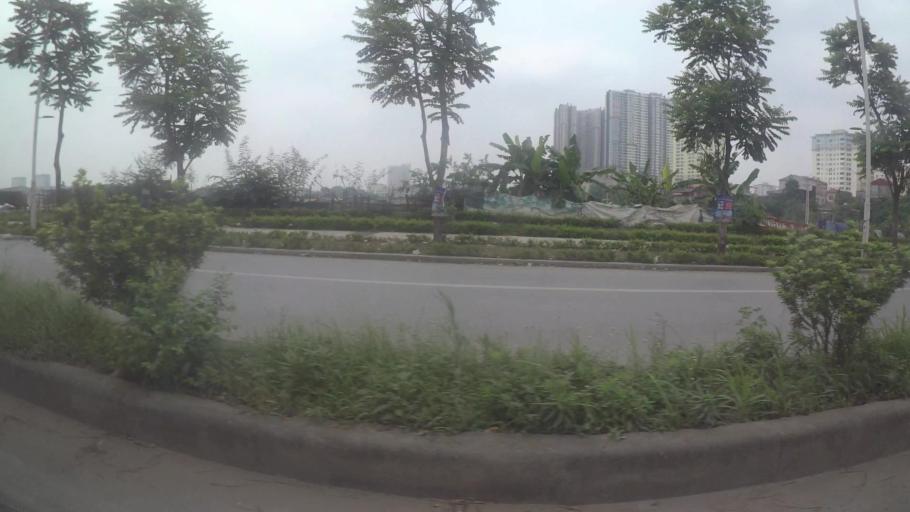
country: VN
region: Ha Noi
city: Cau Dien
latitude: 21.0316
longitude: 105.7567
